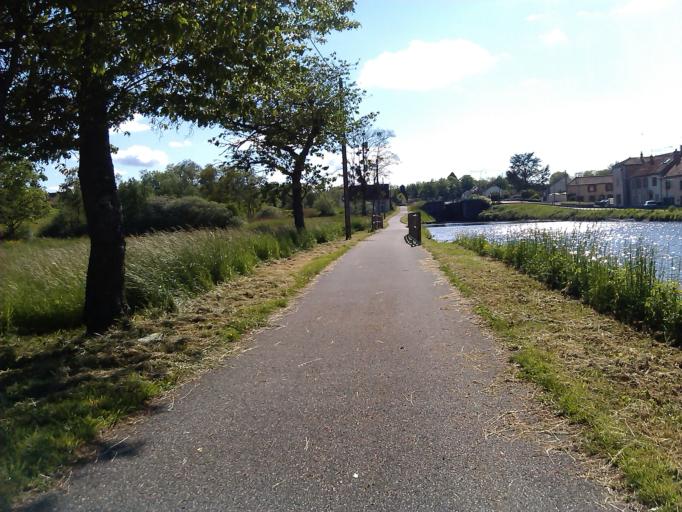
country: FR
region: Bourgogne
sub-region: Departement de Saone-et-Loire
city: Ecuisses
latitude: 46.7571
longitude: 4.5106
